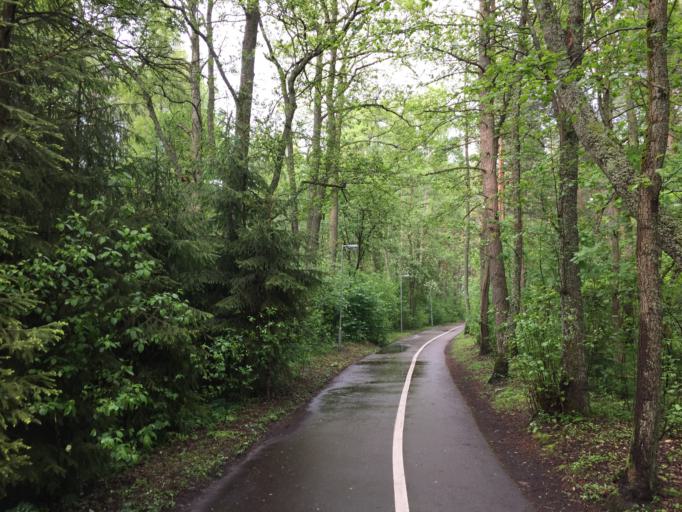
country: LT
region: Klaipedos apskritis
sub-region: Klaipeda
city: Klaipeda
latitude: 55.7526
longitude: 21.1196
